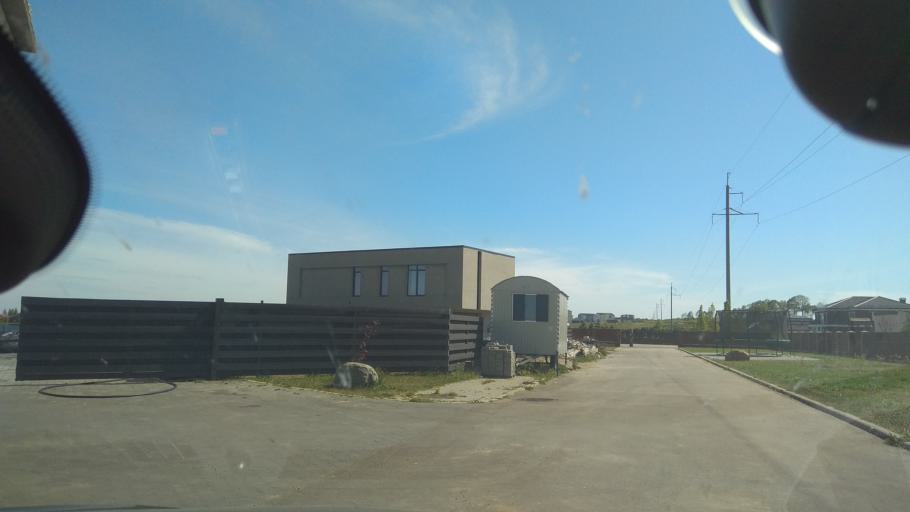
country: LT
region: Klaipedos apskritis
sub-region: Klaipeda
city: Klaipeda
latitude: 55.7485
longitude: 21.1826
